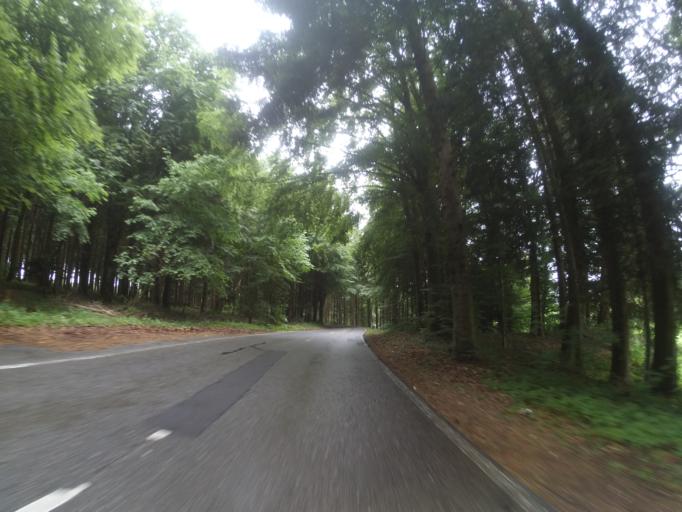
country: DE
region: Baden-Wuerttemberg
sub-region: Tuebingen Region
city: Wangen im Allgau
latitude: 47.7300
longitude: 9.8389
